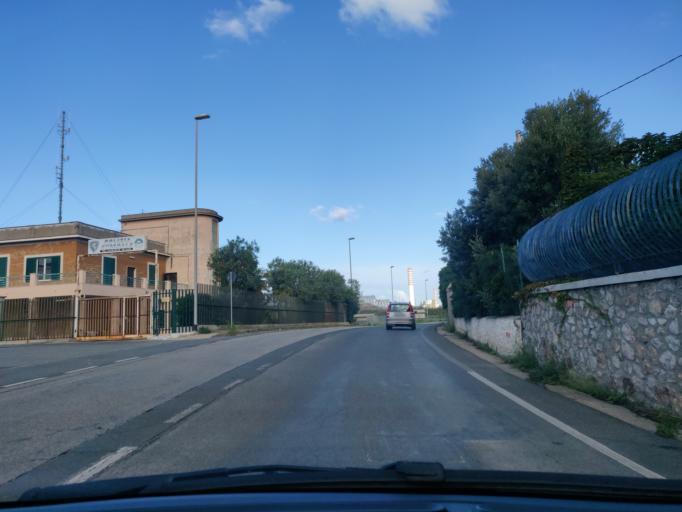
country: IT
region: Latium
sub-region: Citta metropolitana di Roma Capitale
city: Civitavecchia
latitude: 42.1085
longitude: 11.7788
